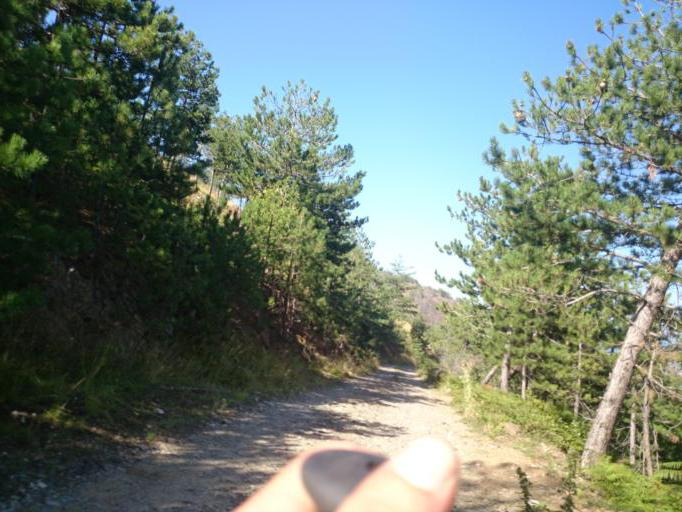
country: AL
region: Diber
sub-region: Rrethi i Bulqizes
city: Martanesh
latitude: 41.4025
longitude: 20.2802
